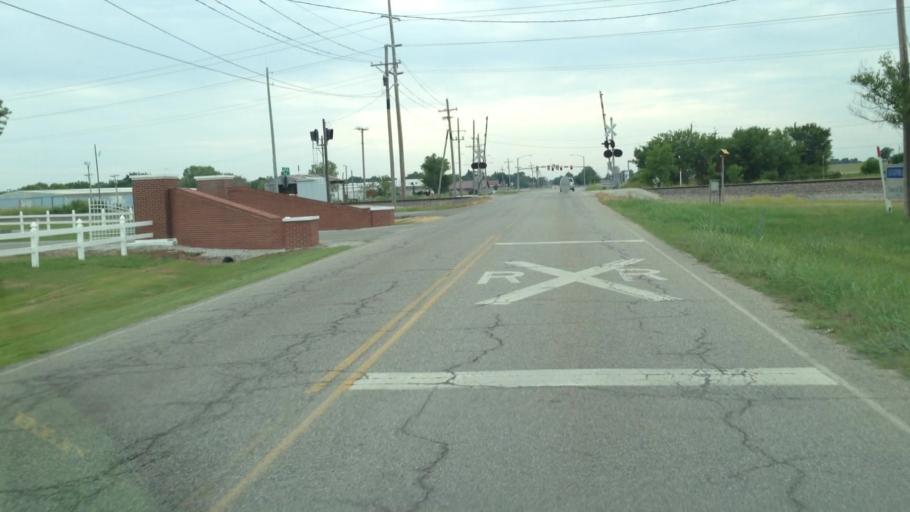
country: US
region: Oklahoma
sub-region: Craig County
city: Vinita
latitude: 36.6560
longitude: -95.1415
